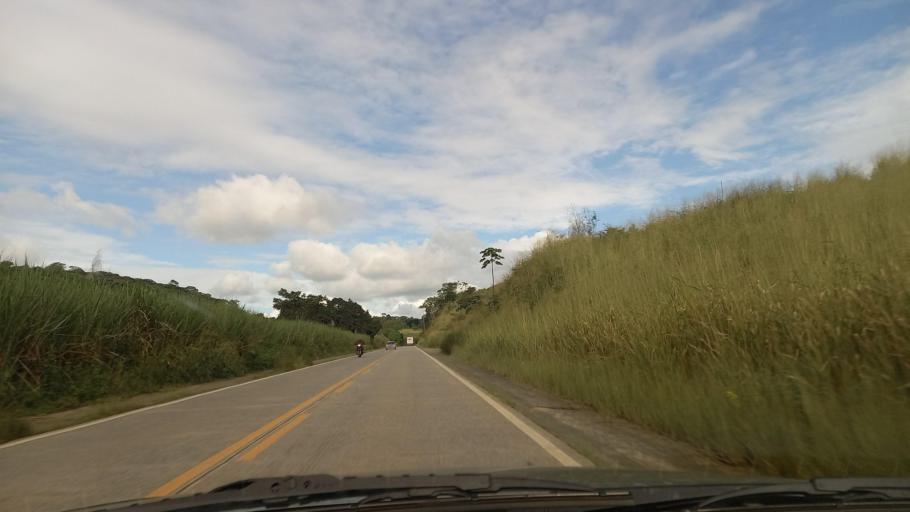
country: BR
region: Pernambuco
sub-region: Catende
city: Catende
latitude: -8.6909
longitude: -35.7022
